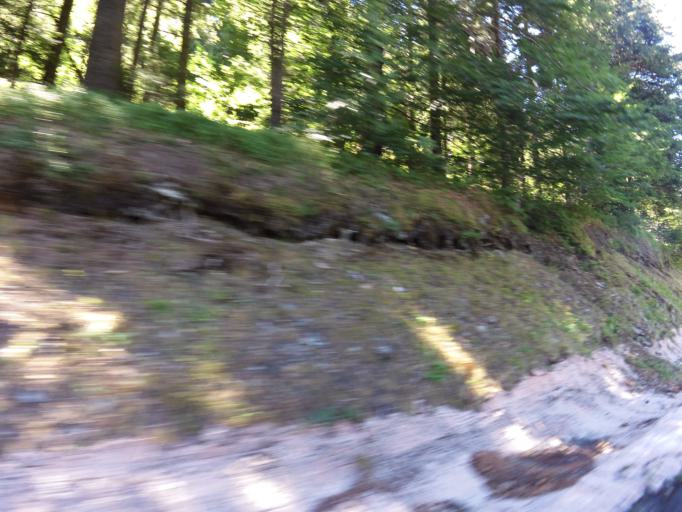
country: FR
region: Languedoc-Roussillon
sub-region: Departement du Gard
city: Valleraugue
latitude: 44.1020
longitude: 3.5429
